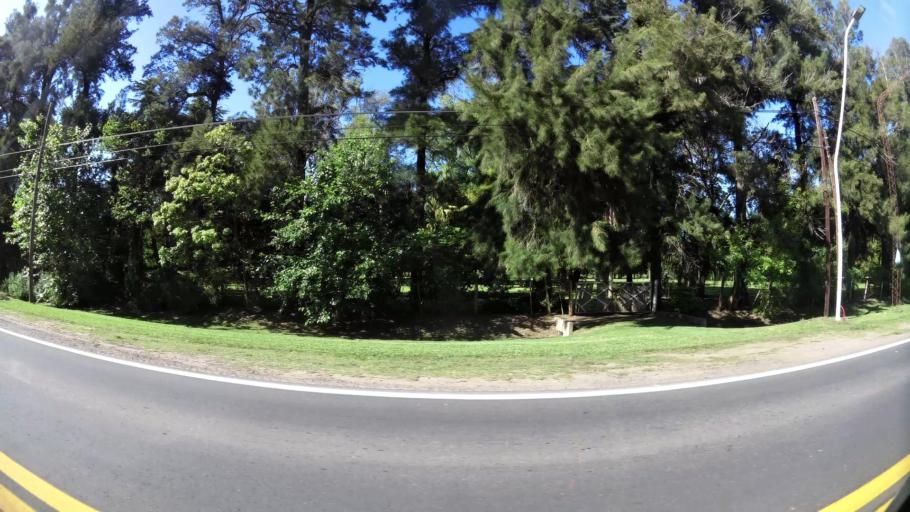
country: AR
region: Santa Fe
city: Esperanza
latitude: -31.4518
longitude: -60.8919
